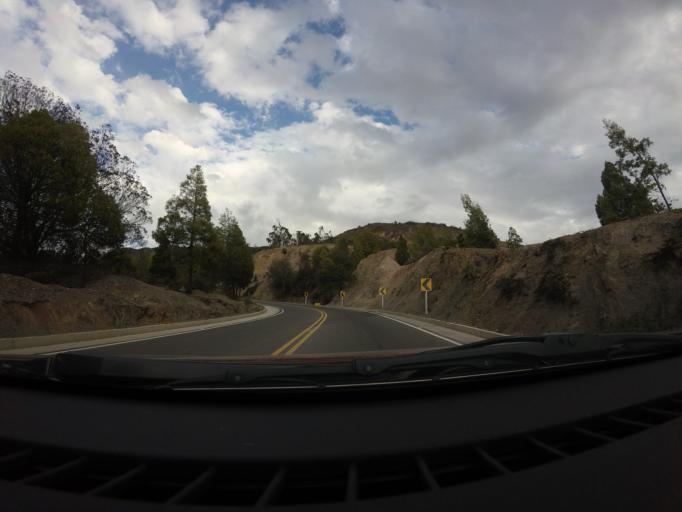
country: CO
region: Boyaca
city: Cucaita
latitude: 5.5486
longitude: -73.4440
